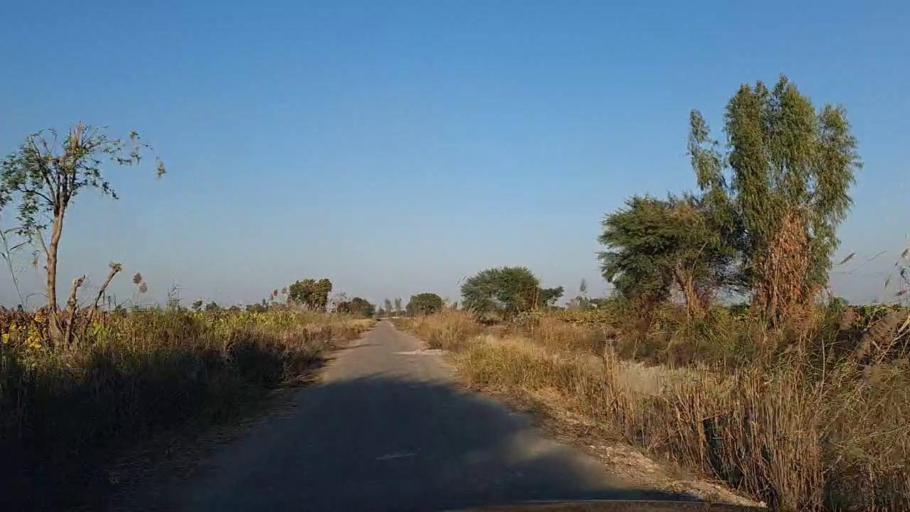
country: PK
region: Sindh
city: Sakrand
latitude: 26.2324
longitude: 68.2775
